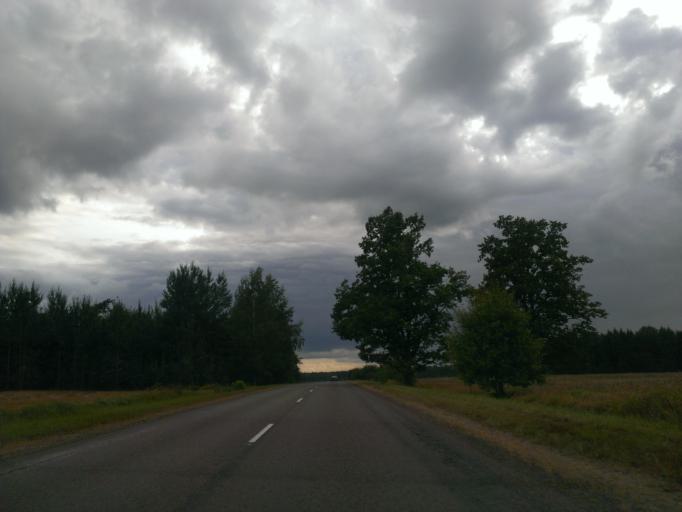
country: LV
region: Kegums
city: Kegums
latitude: 56.7734
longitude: 24.7761
